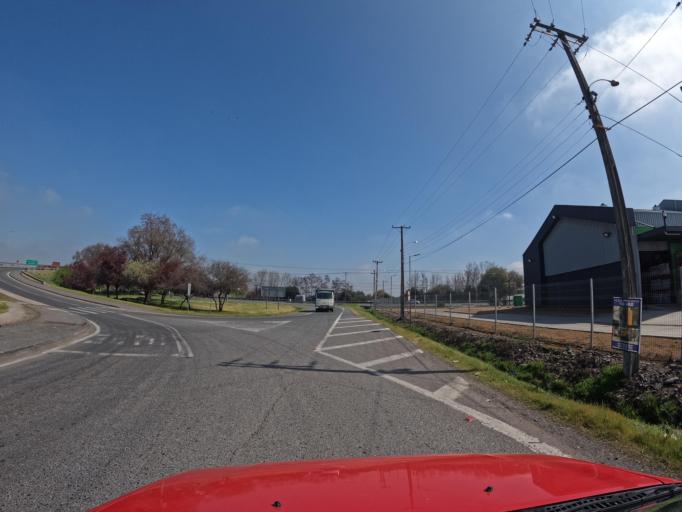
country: CL
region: Maule
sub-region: Provincia de Curico
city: Teno
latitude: -34.9409
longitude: -71.1777
